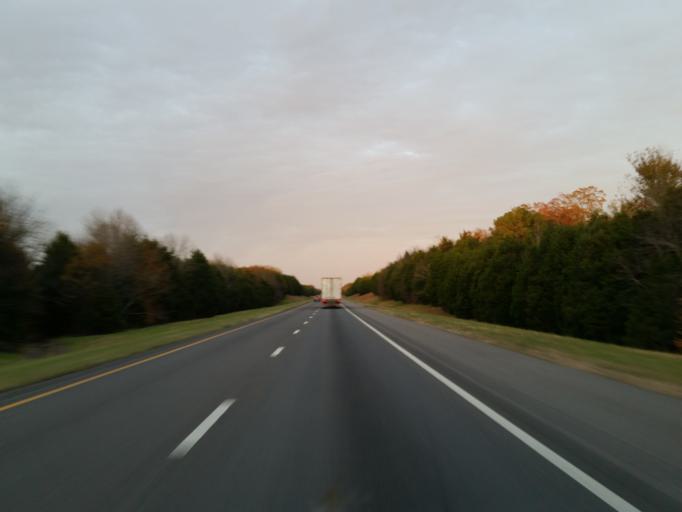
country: US
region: Alabama
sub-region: Sumter County
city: Livingston
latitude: 32.6414
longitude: -88.1983
